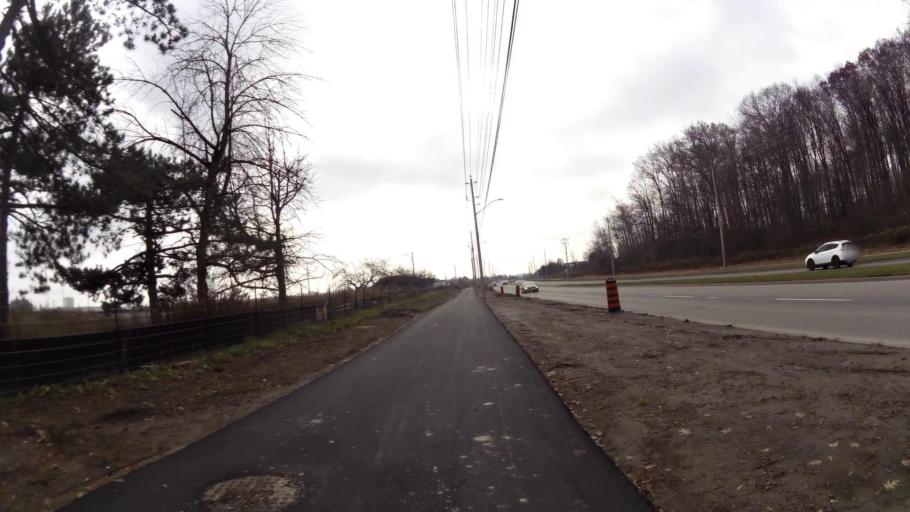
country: CA
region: Ontario
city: Kitchener
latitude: 43.4070
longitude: -80.4585
